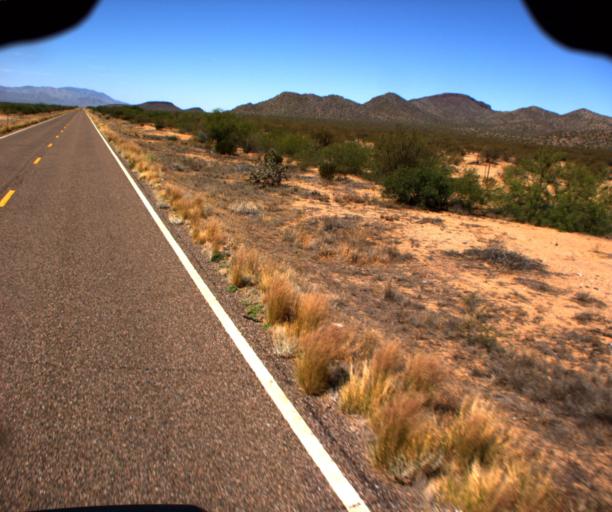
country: US
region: Arizona
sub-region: Yavapai County
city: Congress
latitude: 34.0442
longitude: -113.0663
